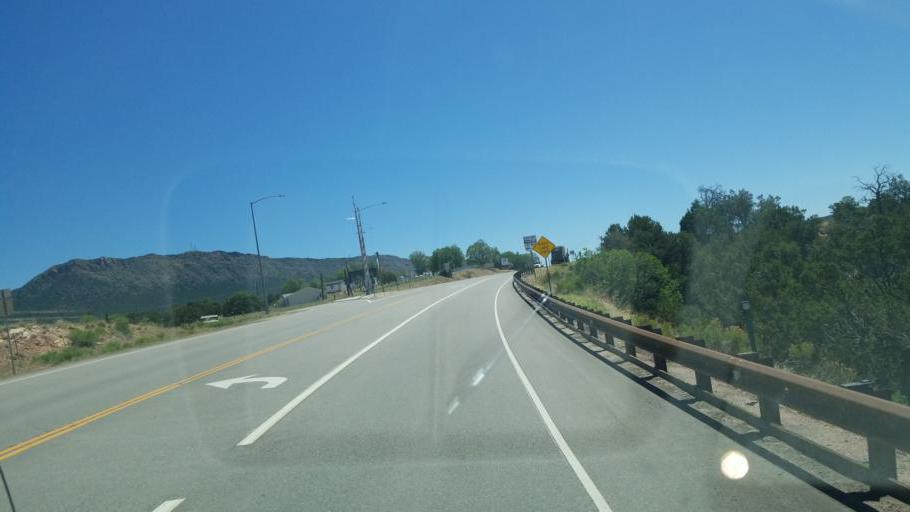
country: US
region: Colorado
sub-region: Fremont County
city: Canon City
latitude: 38.4984
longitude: -105.3517
